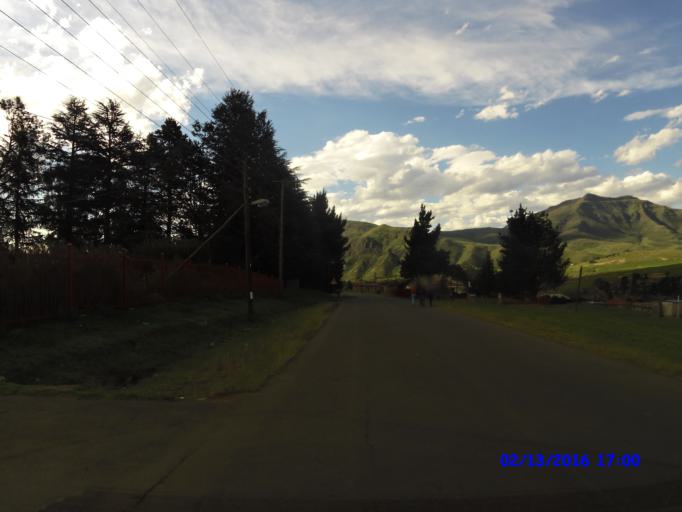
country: LS
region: Qacha's Nek
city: Qacha's Nek
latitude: -30.1155
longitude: 28.6903
